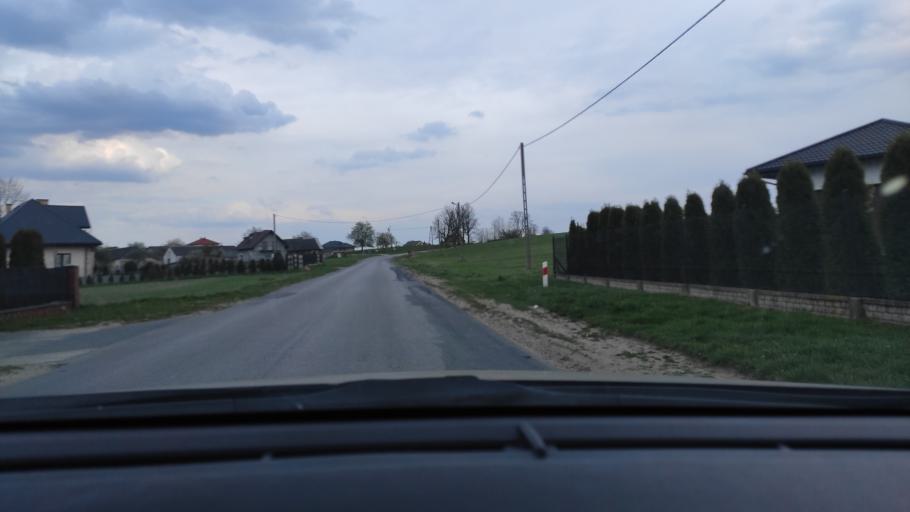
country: PL
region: Masovian Voivodeship
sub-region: Powiat kozienicki
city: Ryczywol
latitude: 51.5956
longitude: 21.3488
